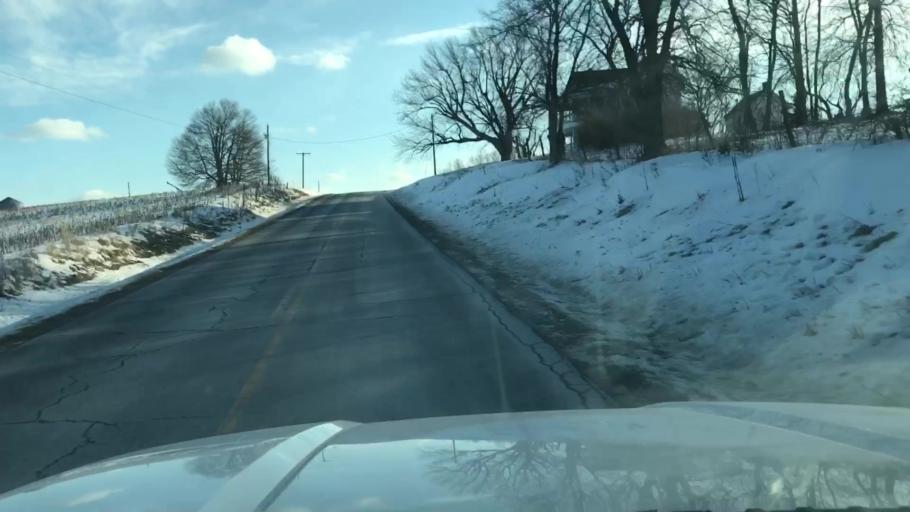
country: US
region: Missouri
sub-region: Holt County
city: Oregon
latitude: 40.0567
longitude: -94.9749
